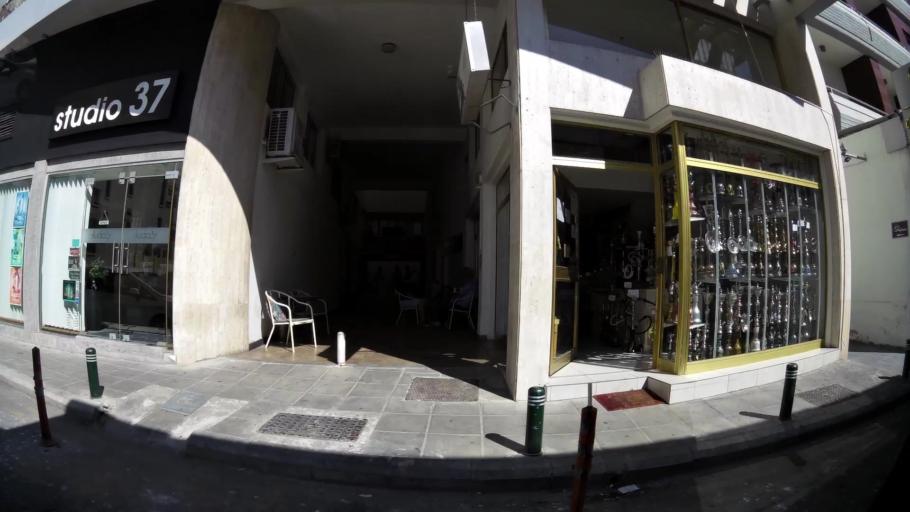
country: CY
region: Larnaka
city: Larnaca
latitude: 34.9136
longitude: 33.6366
